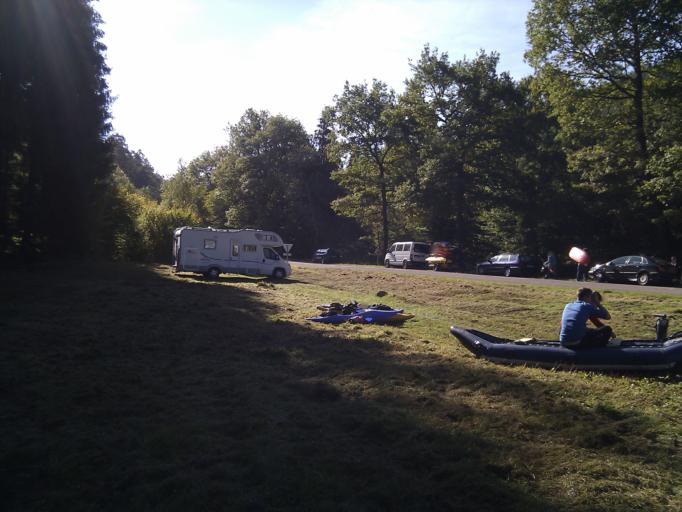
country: FR
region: Bourgogne
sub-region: Departement de la Cote-d'Or
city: Saulieu
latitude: 47.2939
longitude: 4.0340
